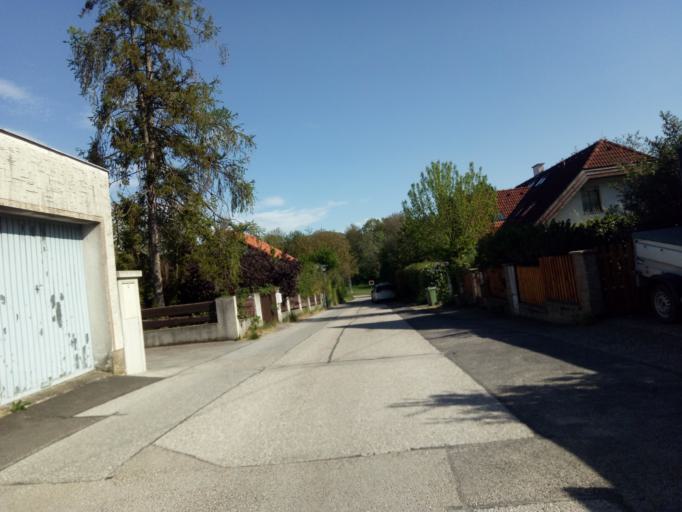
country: AT
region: Lower Austria
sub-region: Politischer Bezirk Modling
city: Laab im Walde
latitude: 48.1400
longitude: 16.1896
